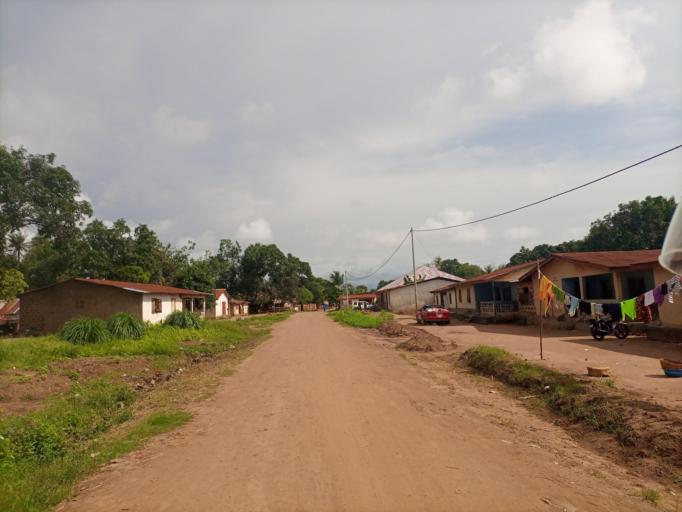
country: SL
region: Northern Province
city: Masoyila
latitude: 8.6129
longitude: -13.1712
